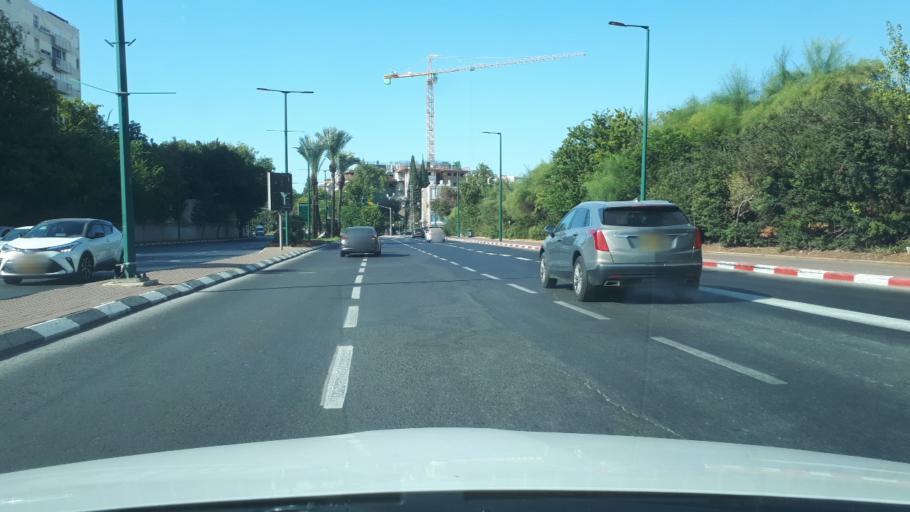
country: IL
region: Tel Aviv
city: Giv`atayim
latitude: 32.0600
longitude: 34.8211
